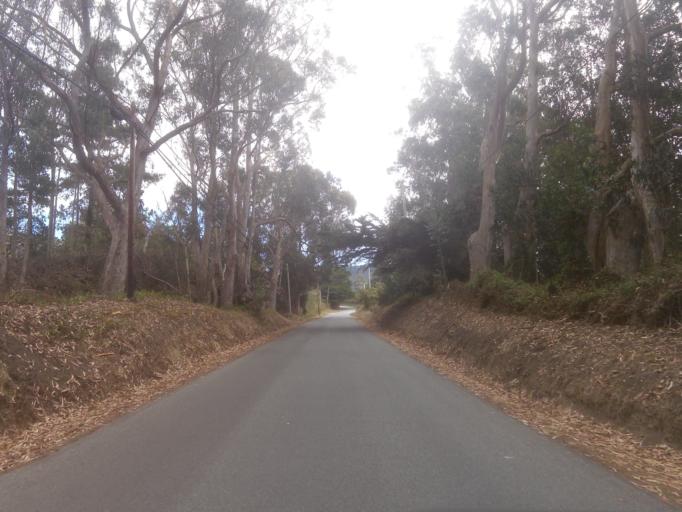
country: US
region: California
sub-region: San Mateo County
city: Half Moon Bay
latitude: 37.4046
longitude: -122.4185
